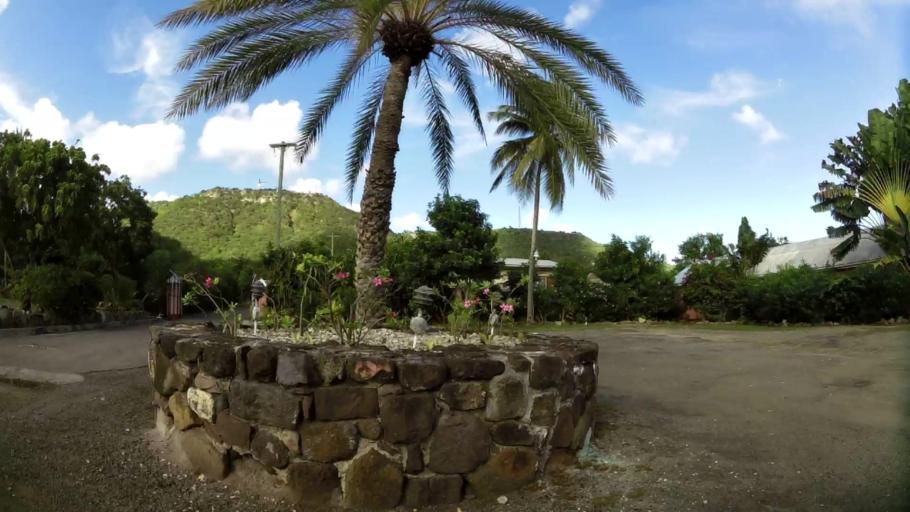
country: AG
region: Saint Paul
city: Falmouth
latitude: 17.0229
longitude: -61.7763
